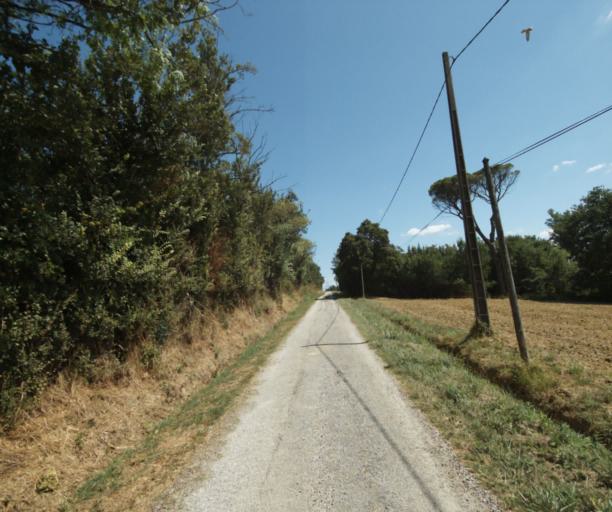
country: FR
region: Midi-Pyrenees
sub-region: Departement de la Haute-Garonne
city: Saint-Felix-Lauragais
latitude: 43.4918
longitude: 1.8845
